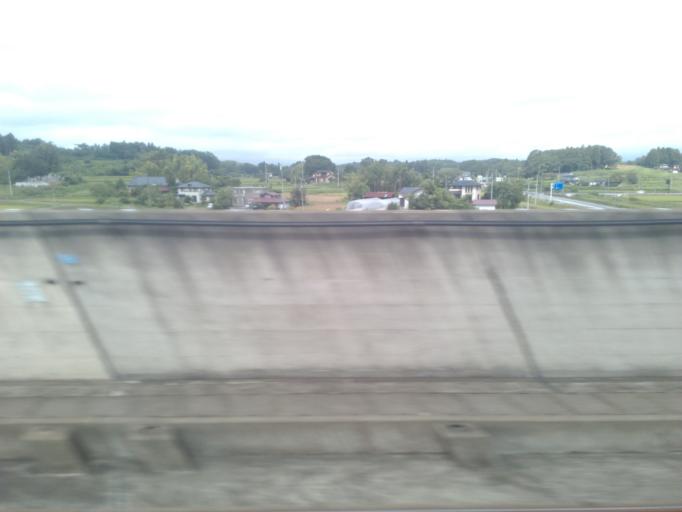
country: JP
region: Fukushima
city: Sukagawa
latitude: 37.2754
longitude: 140.3211
